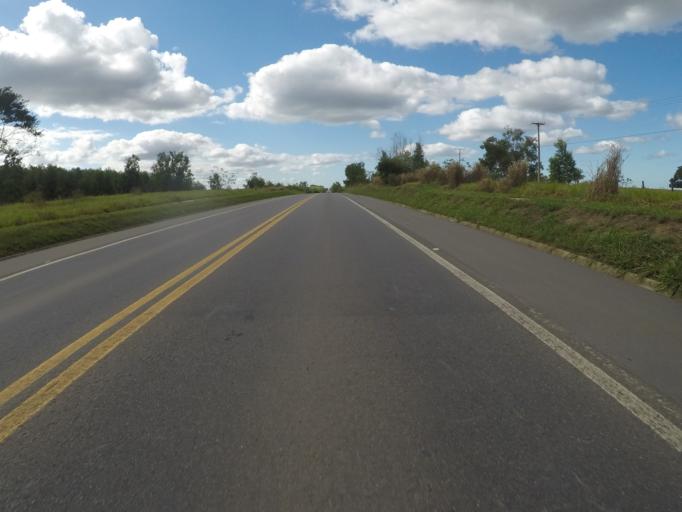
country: BR
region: Espirito Santo
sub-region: Linhares
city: Linhares
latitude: -19.1746
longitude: -40.0903
